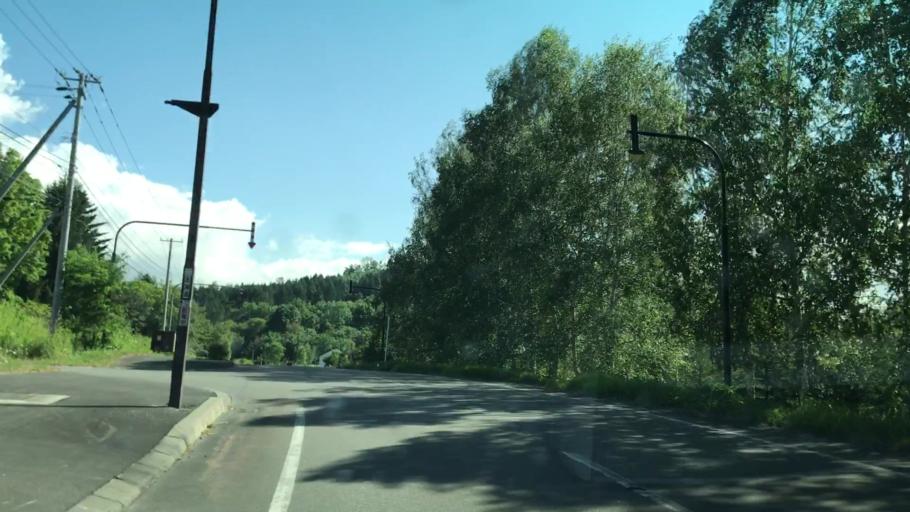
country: JP
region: Hokkaido
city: Shimo-furano
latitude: 42.8667
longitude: 142.4400
